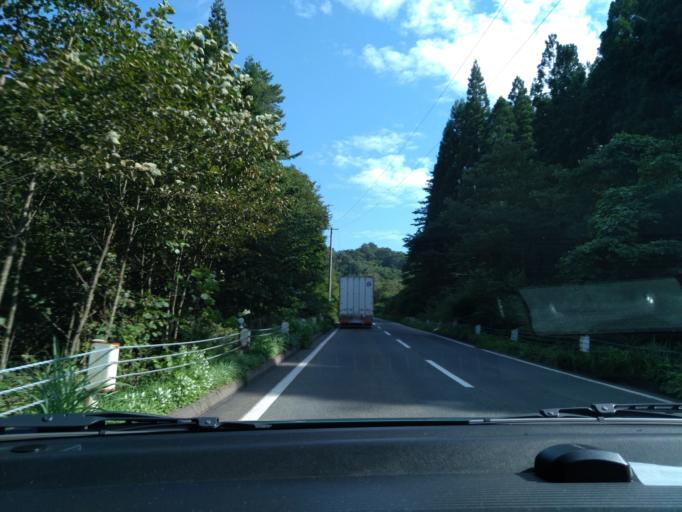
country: JP
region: Iwate
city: Shizukuishi
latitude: 39.6391
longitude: 141.0162
